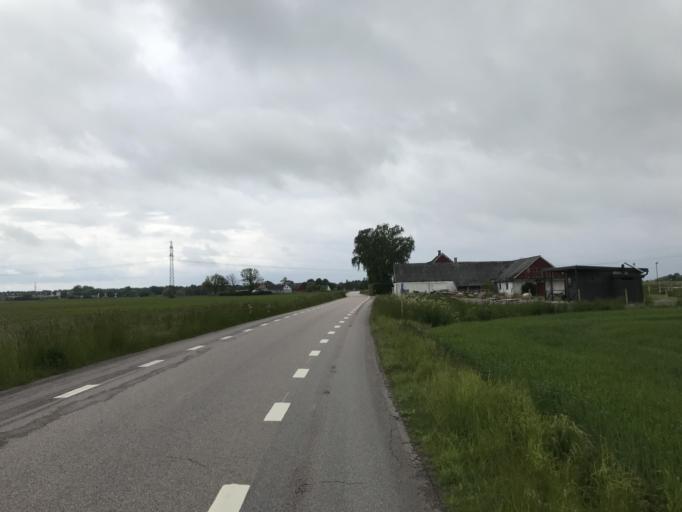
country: SE
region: Skane
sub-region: Landskrona
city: Asmundtorp
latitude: 55.8650
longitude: 12.9252
